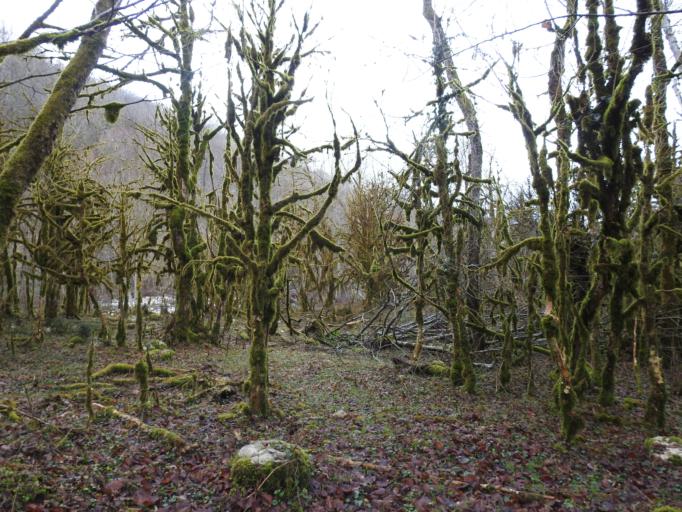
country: GE
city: Gantiadi
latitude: 43.4280
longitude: 40.1295
